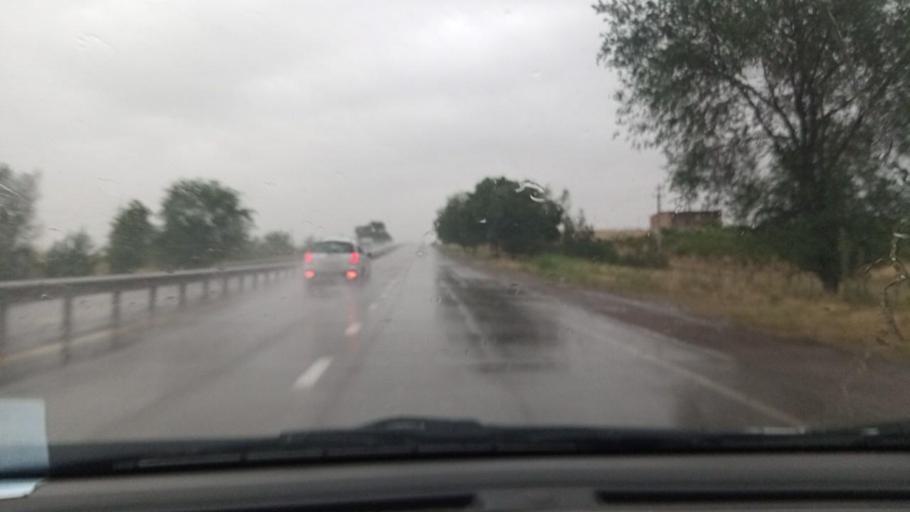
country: UZ
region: Toshkent
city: Ohangaron
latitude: 40.9521
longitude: 69.5686
